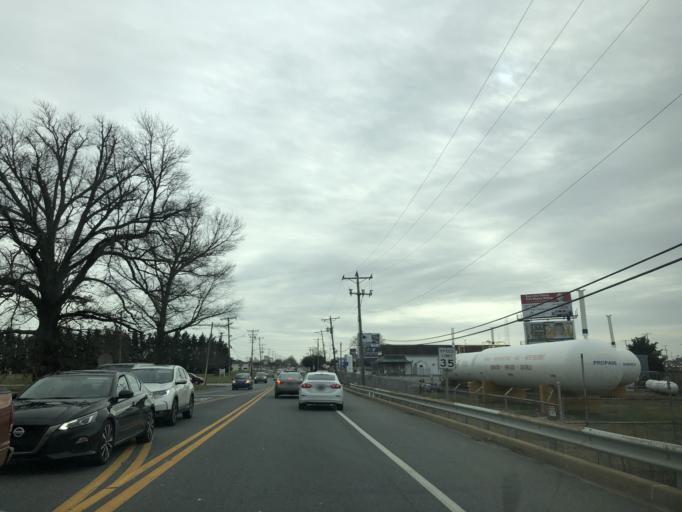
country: US
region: Delaware
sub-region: New Castle County
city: Middletown
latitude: 39.4624
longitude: -75.7210
